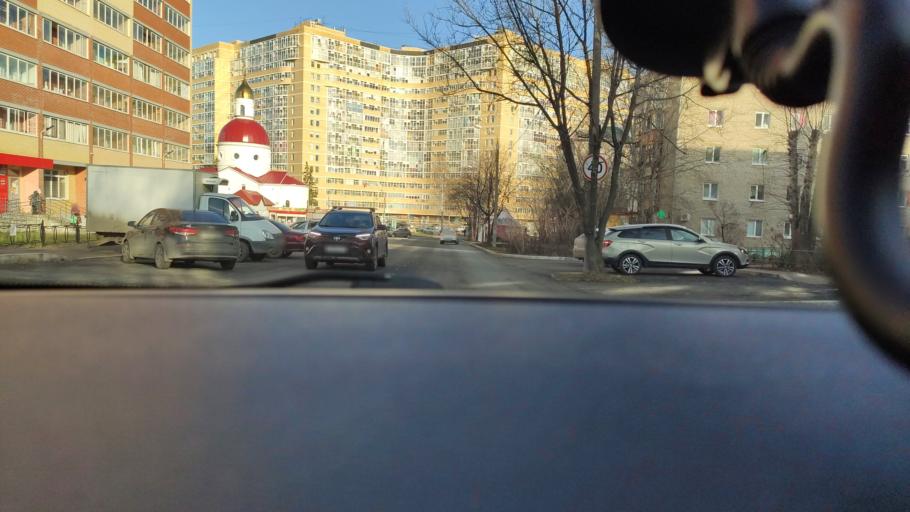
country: RU
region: Perm
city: Kondratovo
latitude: 58.0476
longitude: 56.0871
